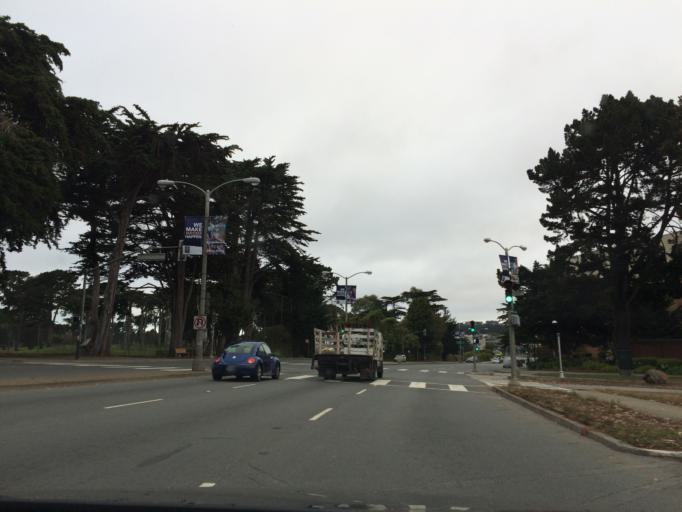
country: US
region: California
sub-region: San Mateo County
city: Daly City
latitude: 37.7236
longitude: -122.4850
